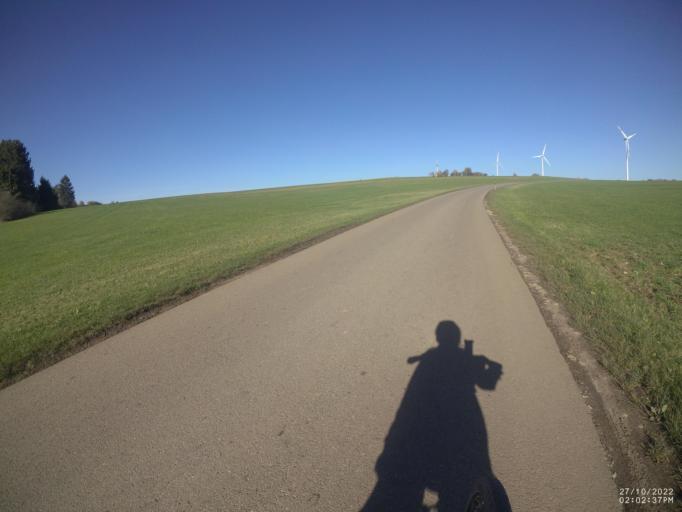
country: DE
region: Baden-Wuerttemberg
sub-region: Regierungsbezirk Stuttgart
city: Deggingen
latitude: 48.5728
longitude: 9.7410
